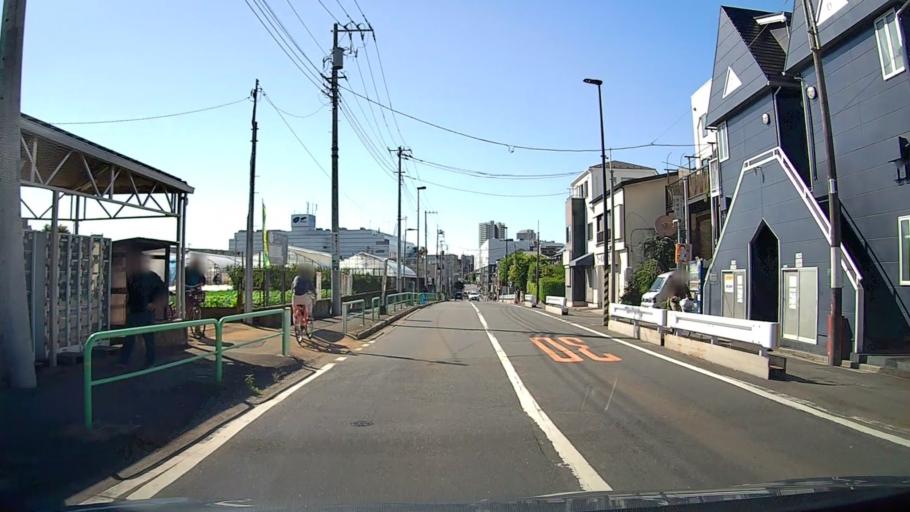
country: JP
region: Saitama
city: Wako
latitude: 35.7544
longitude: 139.5980
